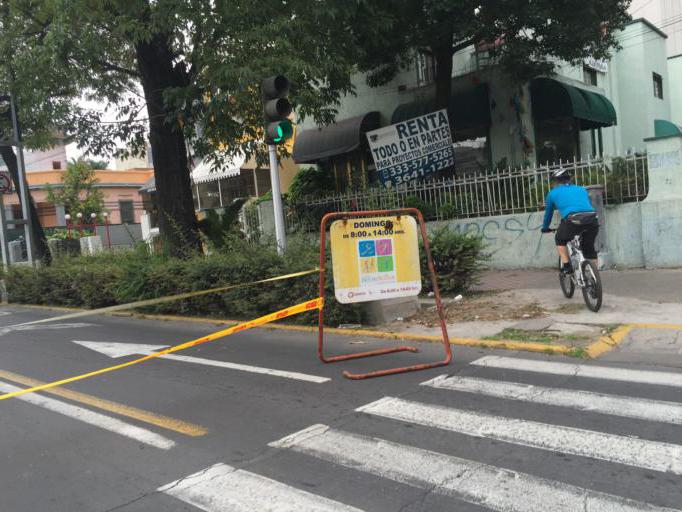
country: MX
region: Jalisco
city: Guadalajara
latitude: 20.6745
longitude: -103.3706
